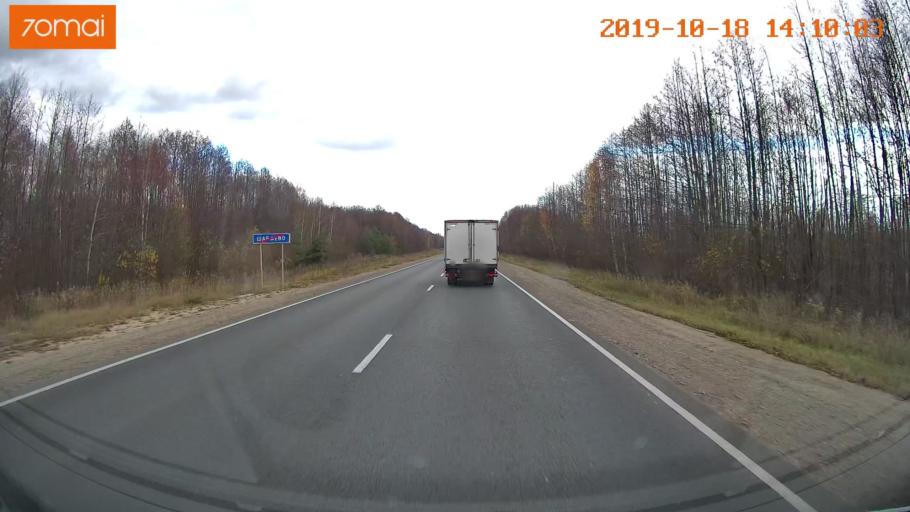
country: RU
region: Rjazan
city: Spas-Klepiki
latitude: 55.1433
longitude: 40.1974
